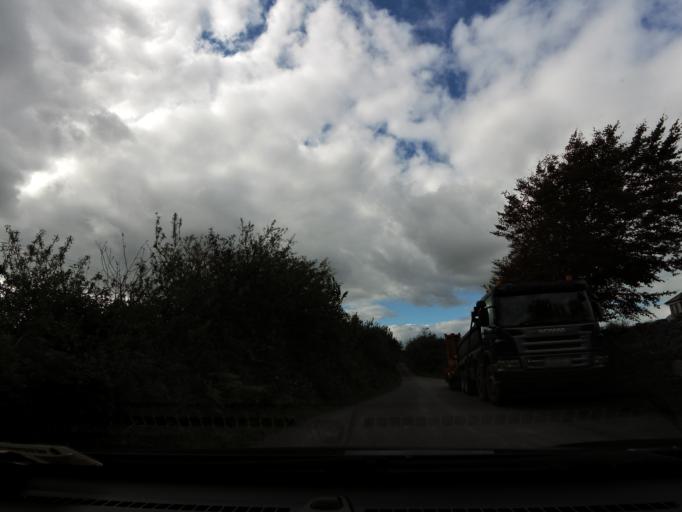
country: IE
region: Connaught
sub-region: County Galway
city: Moycullen
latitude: 53.3319
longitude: -9.1496
